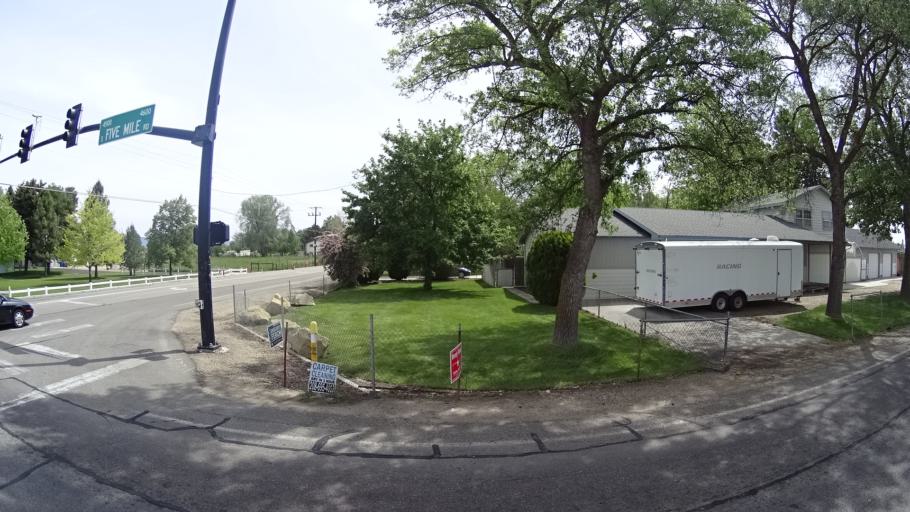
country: US
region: Idaho
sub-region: Ada County
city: Meridian
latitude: 43.5610
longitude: -116.3143
